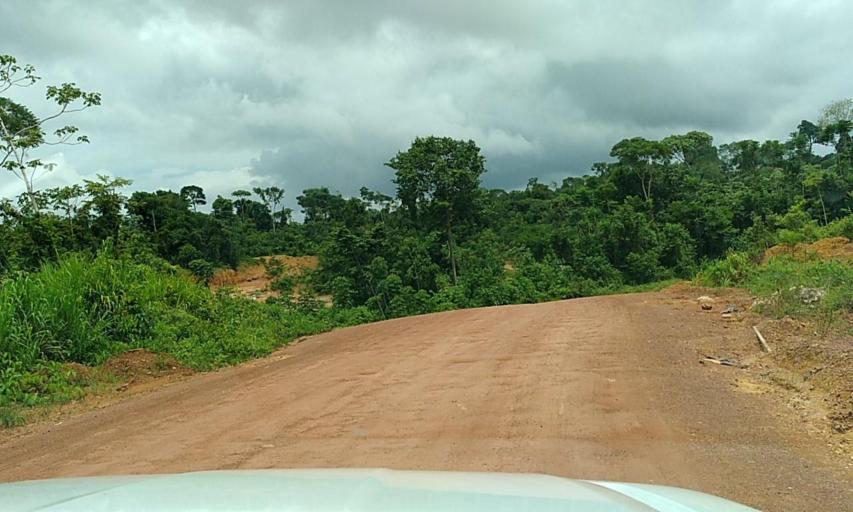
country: BR
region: Para
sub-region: Senador Jose Porfirio
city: Senador Jose Porfirio
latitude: -2.6566
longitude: -51.8437
